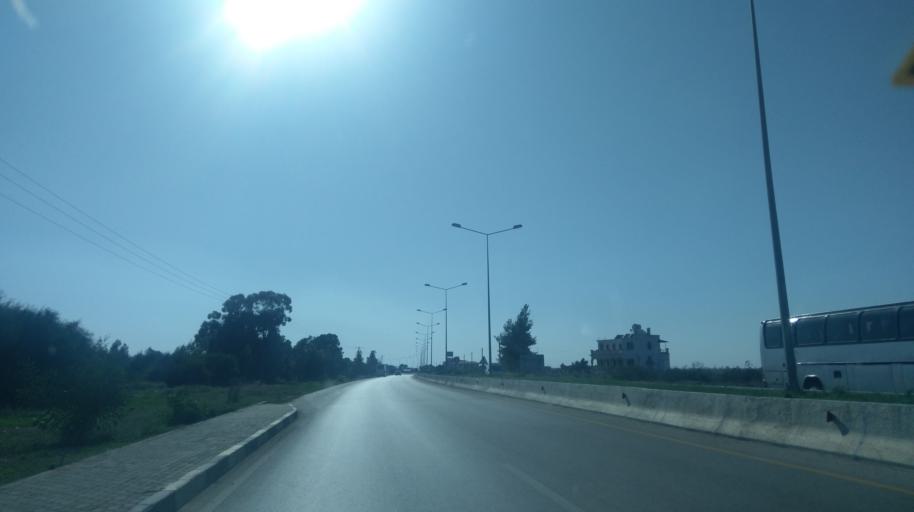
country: CY
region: Ammochostos
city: Trikomo
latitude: 35.2290
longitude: 33.8975
